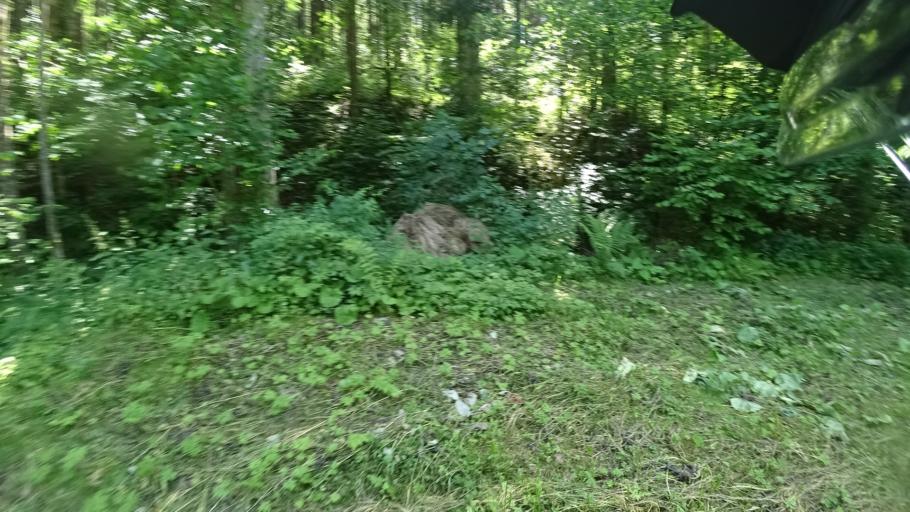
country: SI
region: Osilnica
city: Osilnica
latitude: 45.5134
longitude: 14.6515
